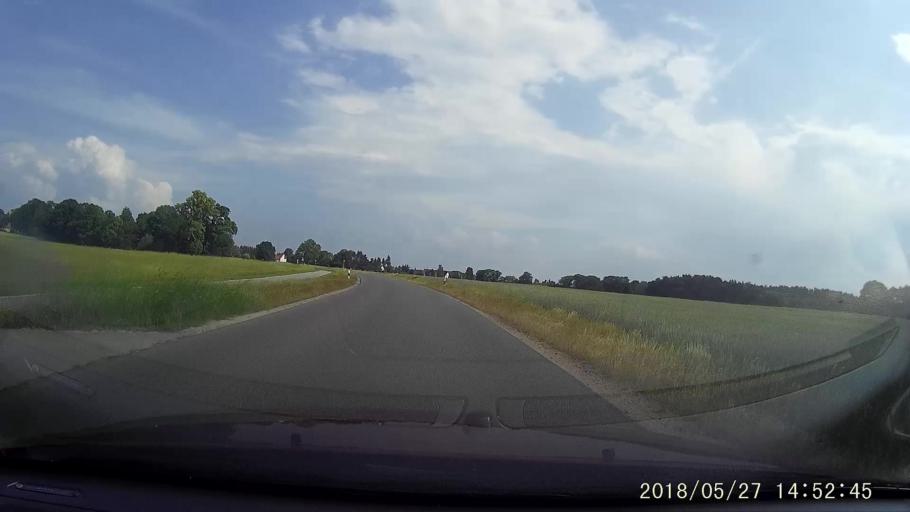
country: DE
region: Saxony
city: Klitten
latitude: 51.3541
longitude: 14.5840
